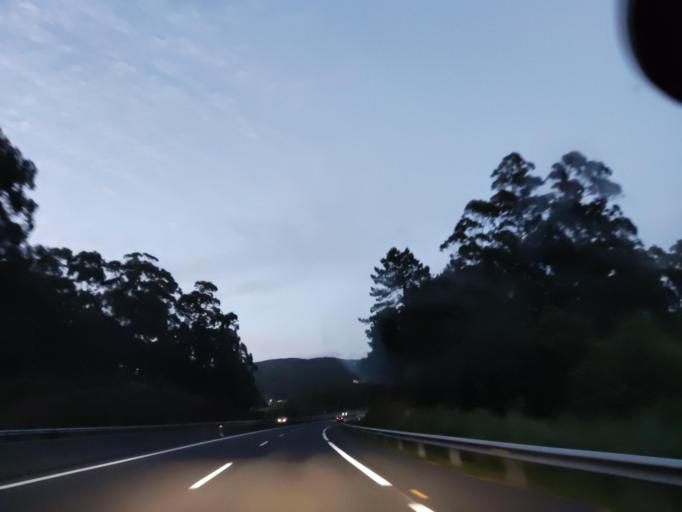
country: ES
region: Galicia
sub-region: Provincia da Coruna
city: Boiro
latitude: 42.6542
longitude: -8.9004
